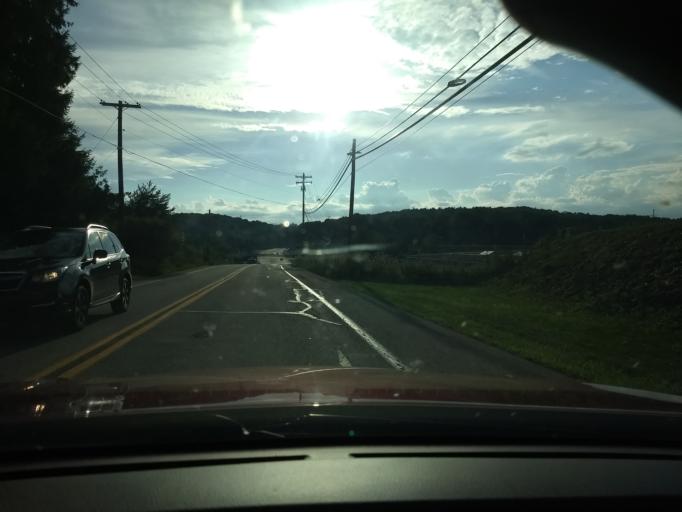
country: US
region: Pennsylvania
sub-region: Armstrong County
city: Freeport
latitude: 40.6673
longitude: -79.7096
